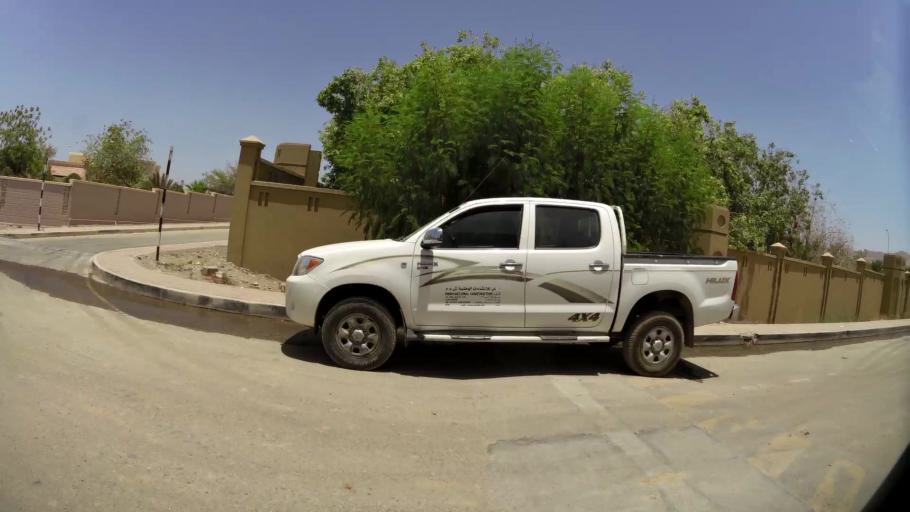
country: OM
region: Muhafazat Masqat
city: Bawshar
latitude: 23.6044
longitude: 58.4777
